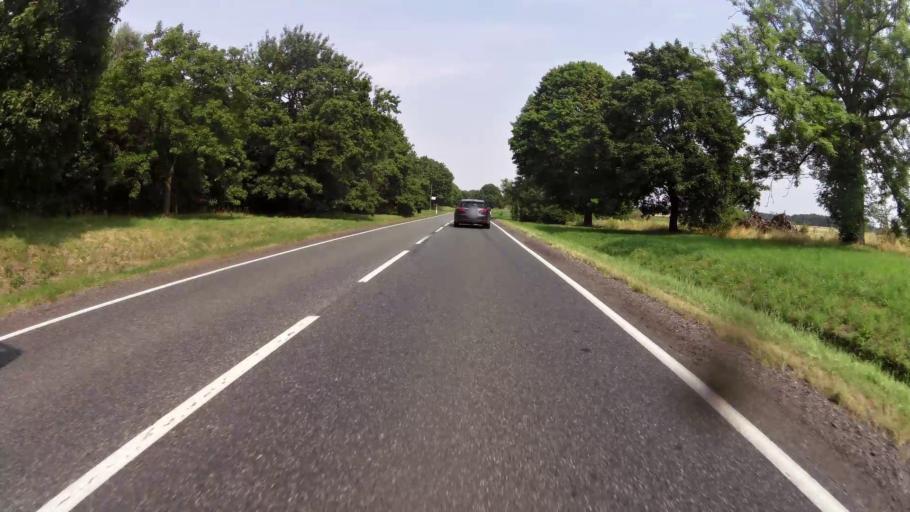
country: PL
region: West Pomeranian Voivodeship
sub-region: Powiat mysliborski
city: Mysliborz
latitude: 52.9360
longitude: 14.9091
